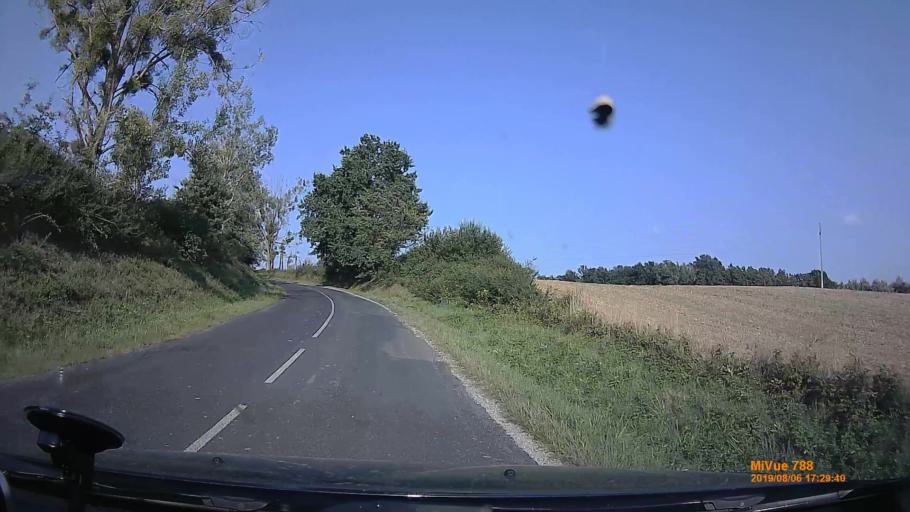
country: HU
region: Zala
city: Murakeresztur
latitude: 46.3970
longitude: 16.8528
